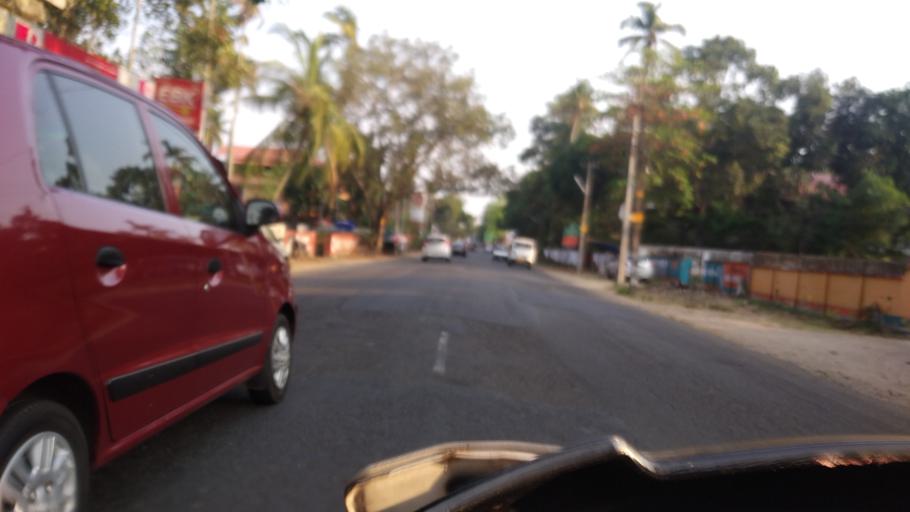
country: IN
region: Kerala
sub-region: Thrissur District
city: Thanniyam
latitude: 10.3804
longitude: 76.1216
